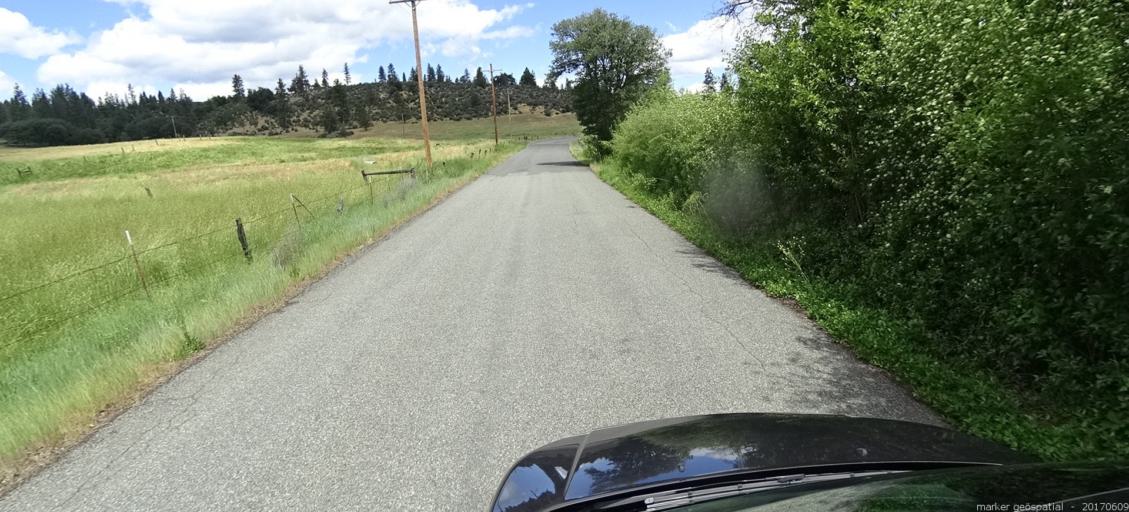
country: US
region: California
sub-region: Siskiyou County
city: Yreka
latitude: 41.4074
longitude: -122.8680
